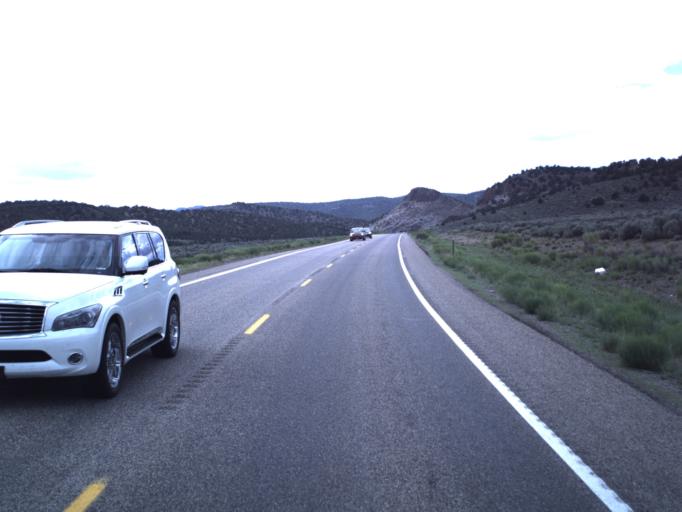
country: US
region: Utah
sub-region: Garfield County
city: Panguitch
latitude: 37.9662
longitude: -112.4230
